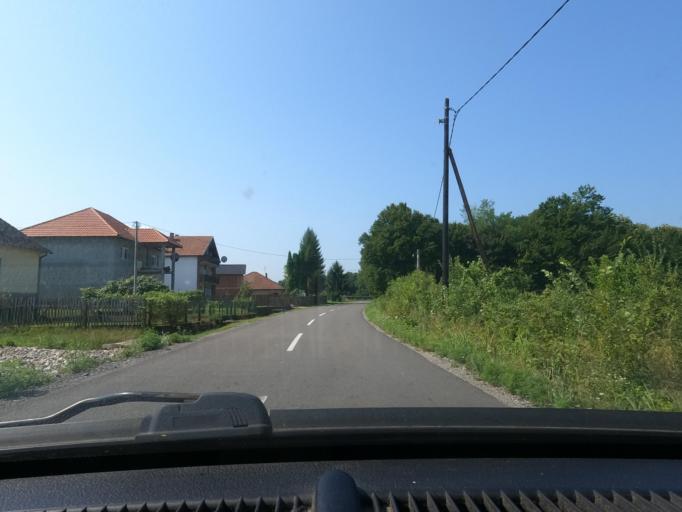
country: RS
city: Kozjak
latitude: 44.5520
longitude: 19.2953
